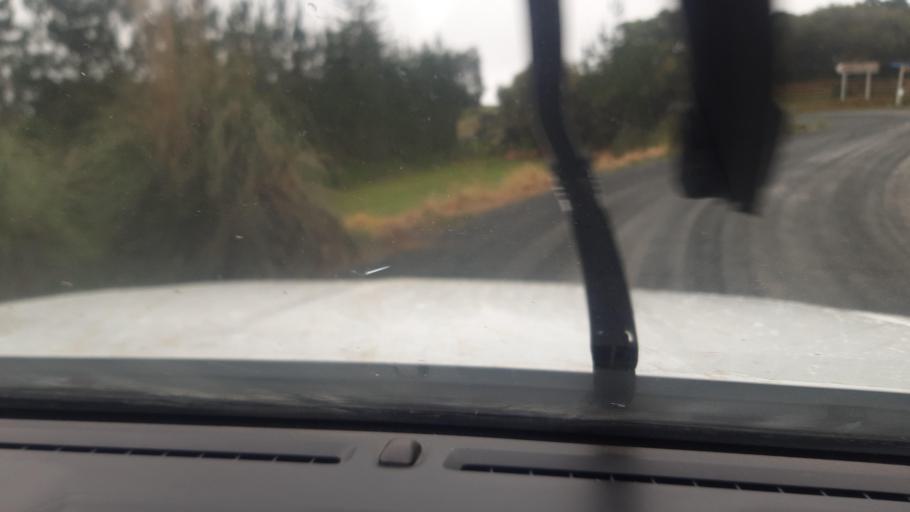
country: NZ
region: Northland
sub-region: Far North District
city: Kaitaia
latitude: -34.9780
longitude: 173.2009
